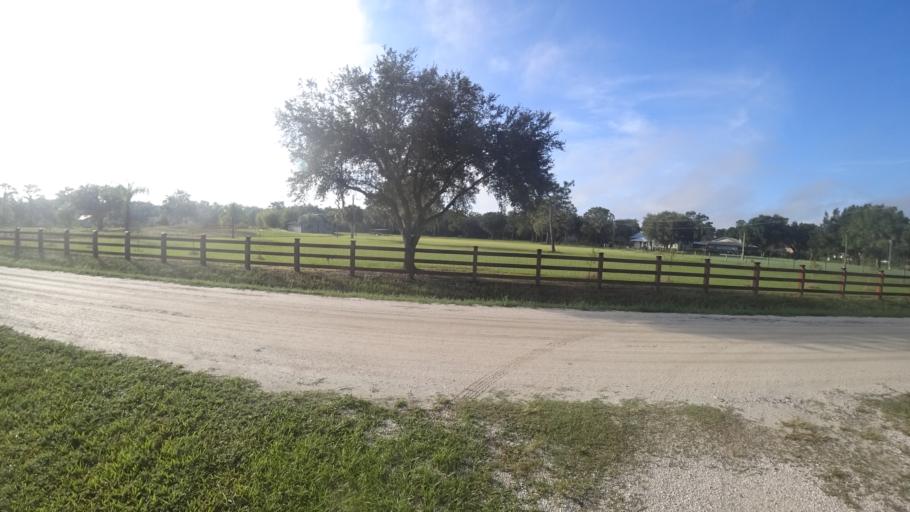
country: US
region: Florida
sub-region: Sarasota County
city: The Meadows
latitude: 27.4128
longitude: -82.3014
